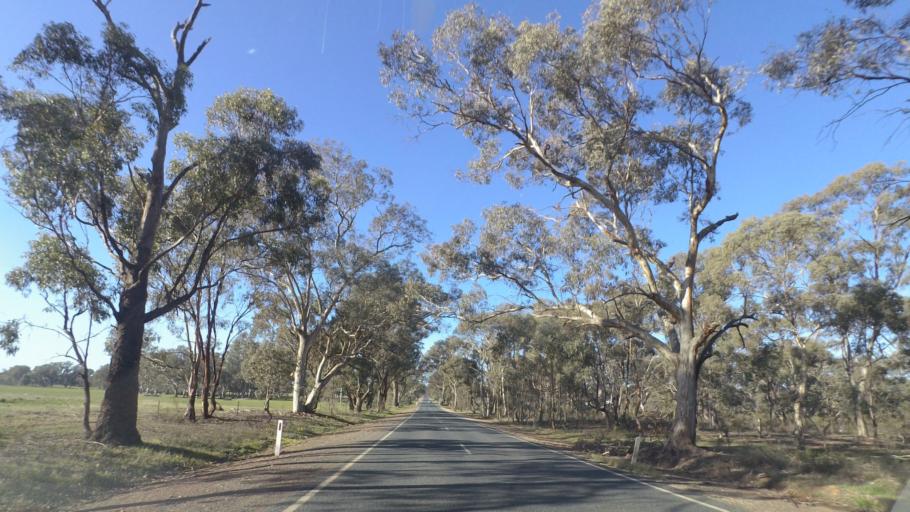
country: AU
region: Victoria
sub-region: Greater Bendigo
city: Epsom
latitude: -36.6758
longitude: 144.3931
